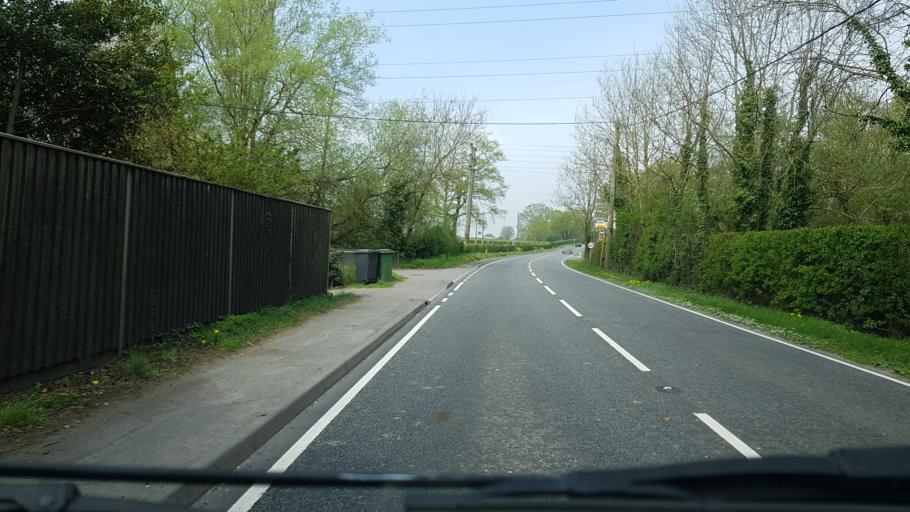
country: GB
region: England
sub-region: Hampshire
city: Kingsclere
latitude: 51.3314
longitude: -1.2542
